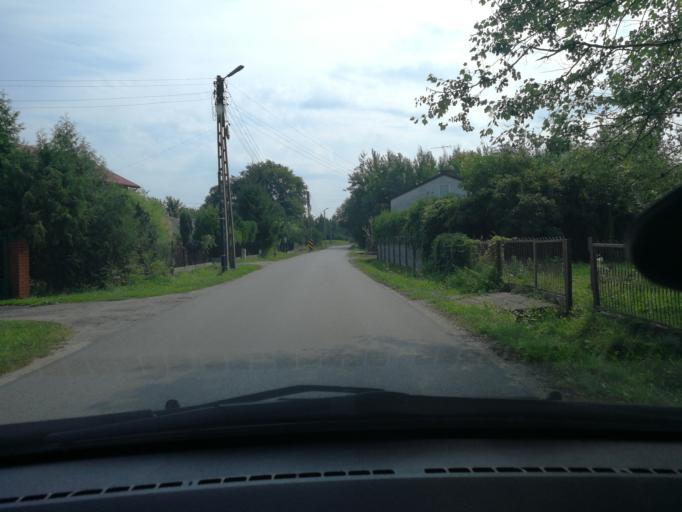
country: PL
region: Lodz Voivodeship
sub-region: Skierniewice
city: Skierniewice
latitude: 51.9745
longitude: 20.1087
